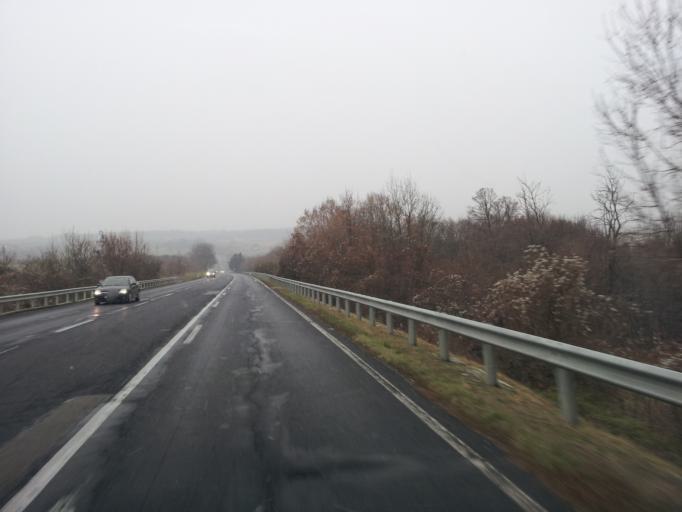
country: HU
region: Veszprem
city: Urkut
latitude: 47.1494
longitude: 17.6663
